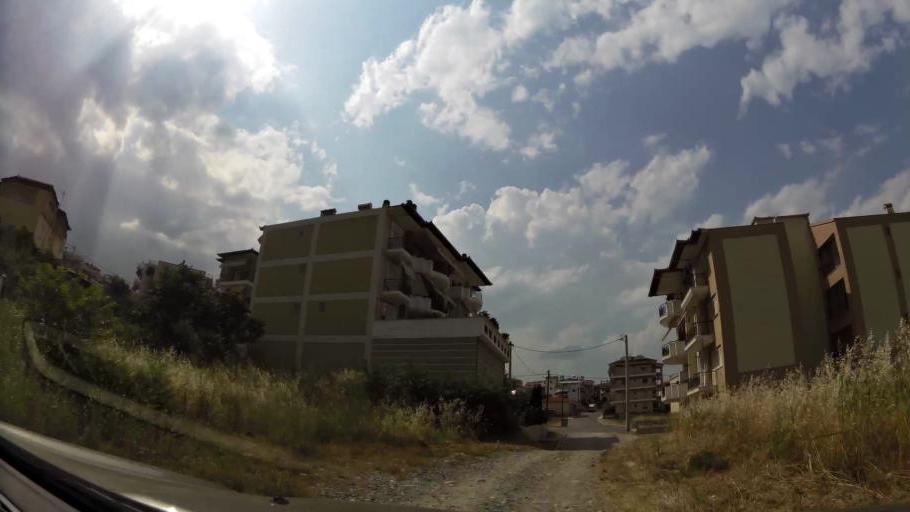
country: GR
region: Central Macedonia
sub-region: Nomos Imathias
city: Veroia
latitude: 40.5153
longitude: 22.2085
